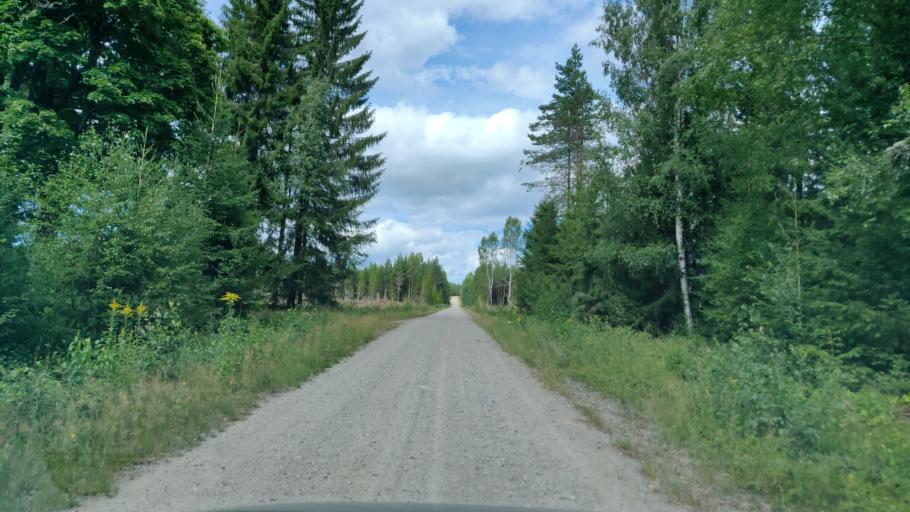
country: SE
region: Vaermland
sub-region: Hagfors Kommun
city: Hagfors
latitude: 60.0061
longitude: 13.7271
